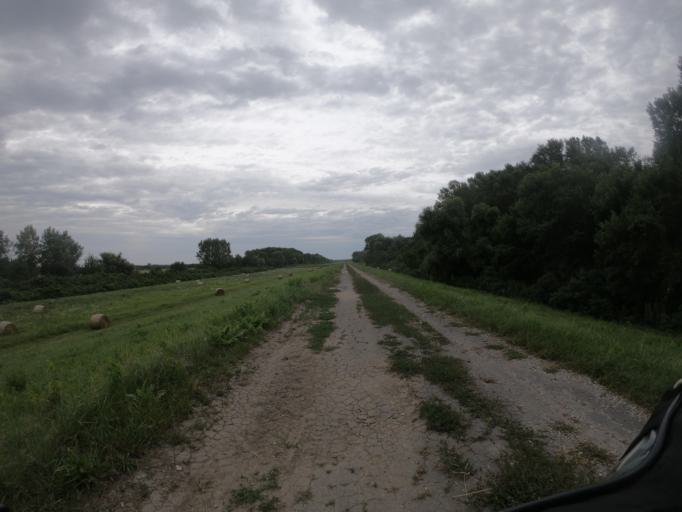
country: HU
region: Hajdu-Bihar
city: Egyek
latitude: 47.6938
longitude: 20.8976
